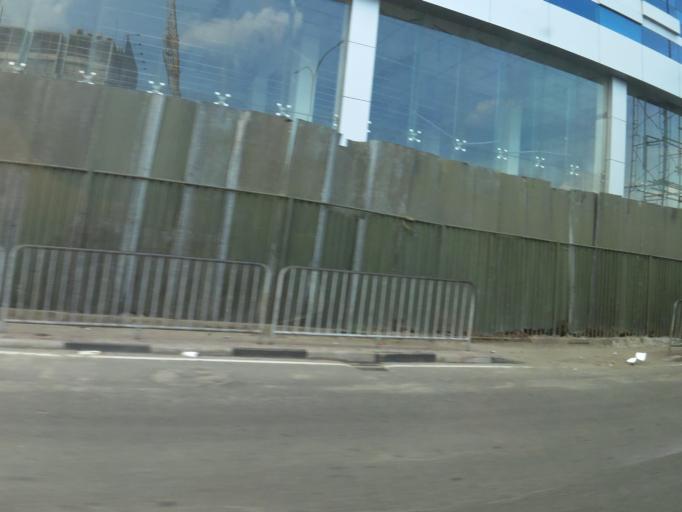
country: LK
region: Western
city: Kolonnawa
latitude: 6.9404
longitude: 79.8782
